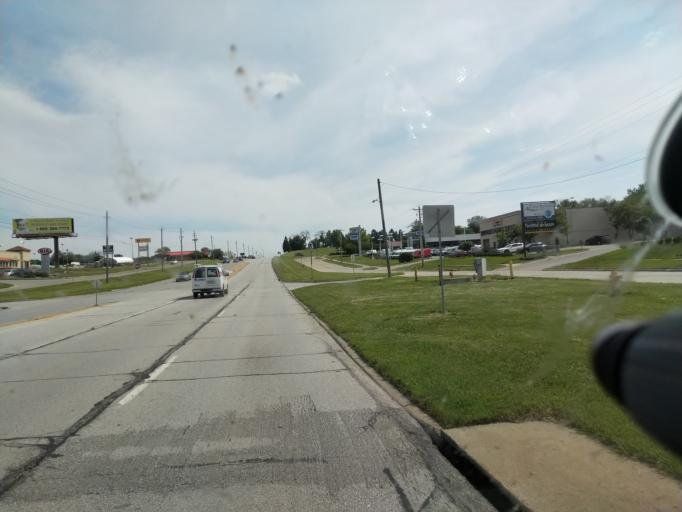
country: US
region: Iowa
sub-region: Polk County
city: Urbandale
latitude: 41.6426
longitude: -93.6978
